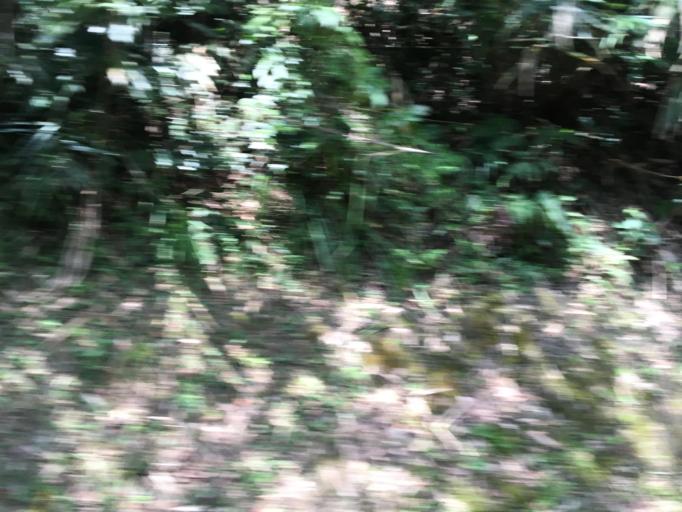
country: TW
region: Taiwan
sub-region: Yilan
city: Yilan
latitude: 24.9329
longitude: 121.6884
